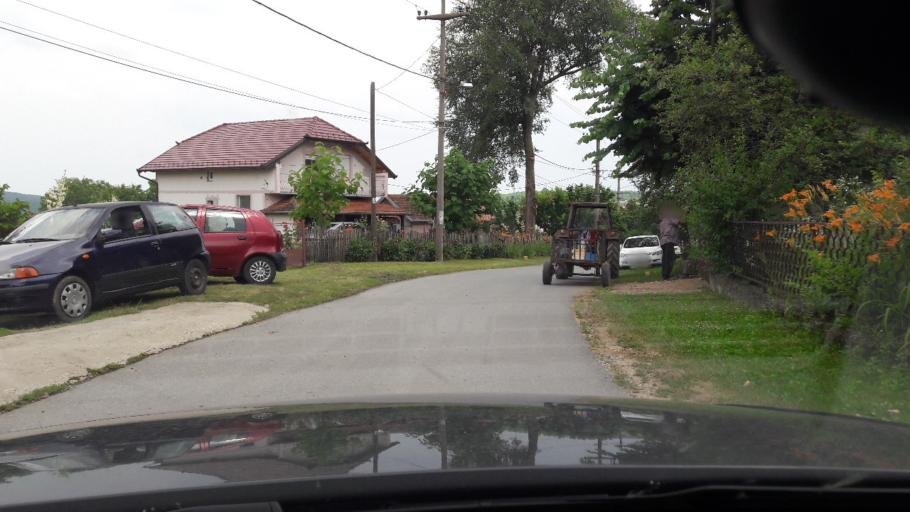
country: RS
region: Central Serbia
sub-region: Belgrade
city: Grocka
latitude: 44.6511
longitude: 20.5997
